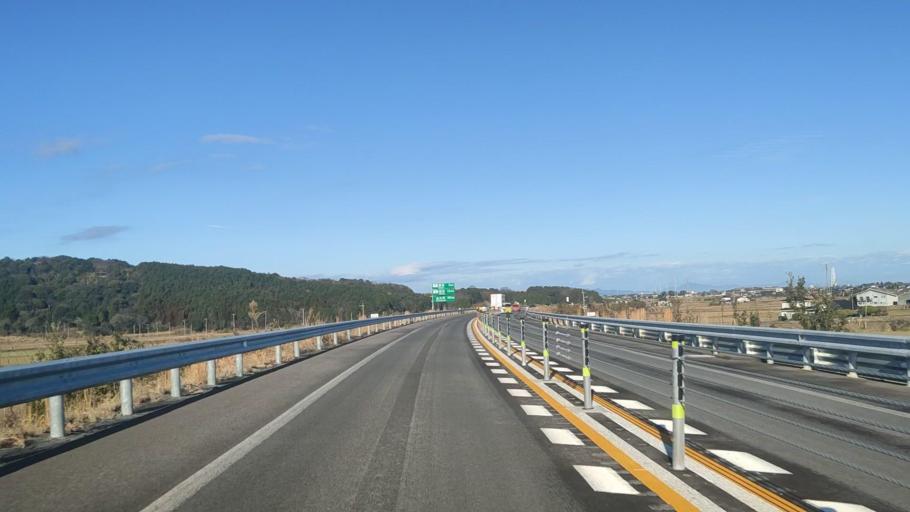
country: JP
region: Fukuoka
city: Yoshitomi
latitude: 33.5655
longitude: 131.1532
